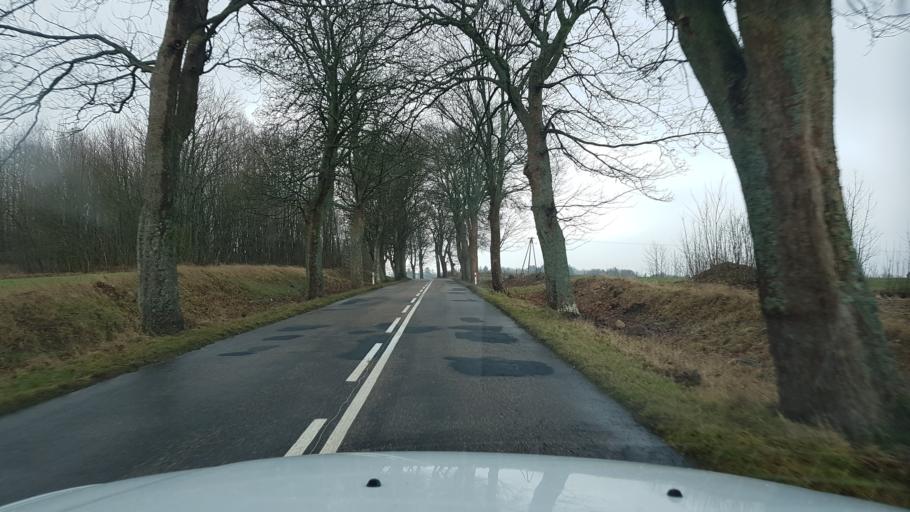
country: PL
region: West Pomeranian Voivodeship
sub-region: Powiat drawski
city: Czaplinek
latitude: 53.5741
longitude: 16.2338
